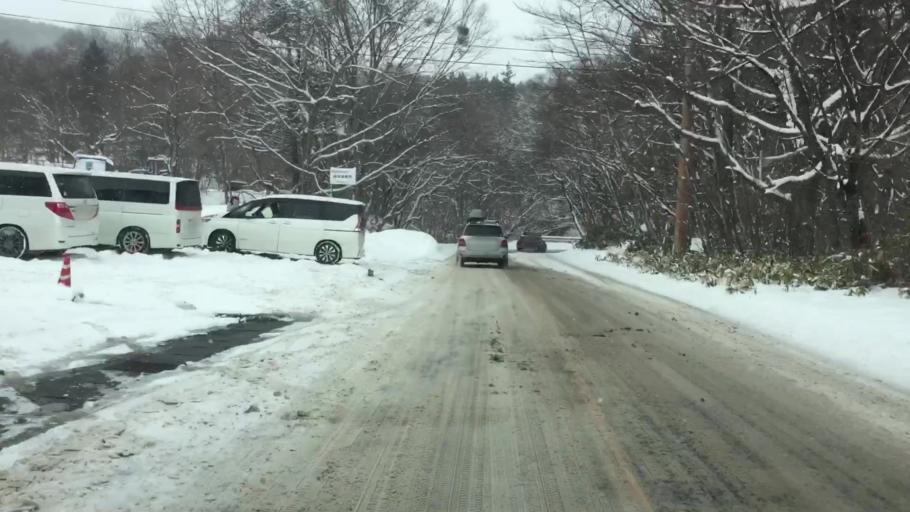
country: JP
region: Tochigi
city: Yaita
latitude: 36.9536
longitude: 139.7724
